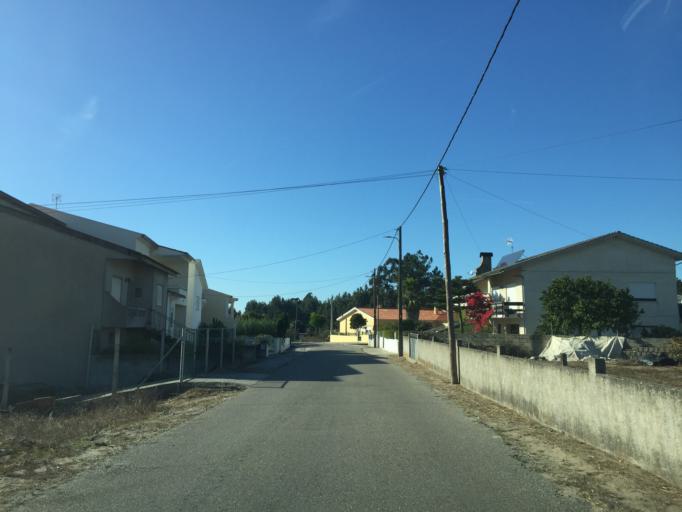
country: PT
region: Coimbra
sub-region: Figueira da Foz
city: Tavarede
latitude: 40.2176
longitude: -8.8539
